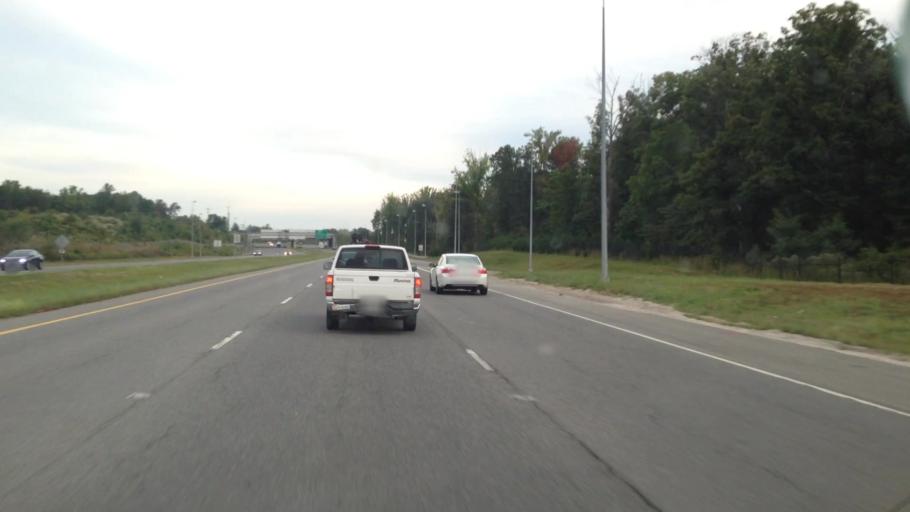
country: US
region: Virginia
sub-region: Fairfax County
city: West Springfield
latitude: 38.7484
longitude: -77.2101
